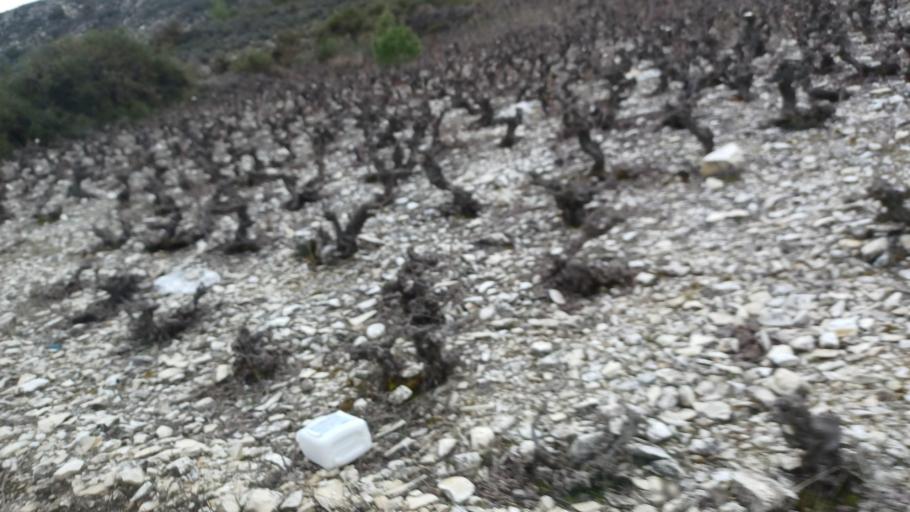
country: CY
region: Limassol
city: Pachna
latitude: 34.8689
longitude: 32.7996
